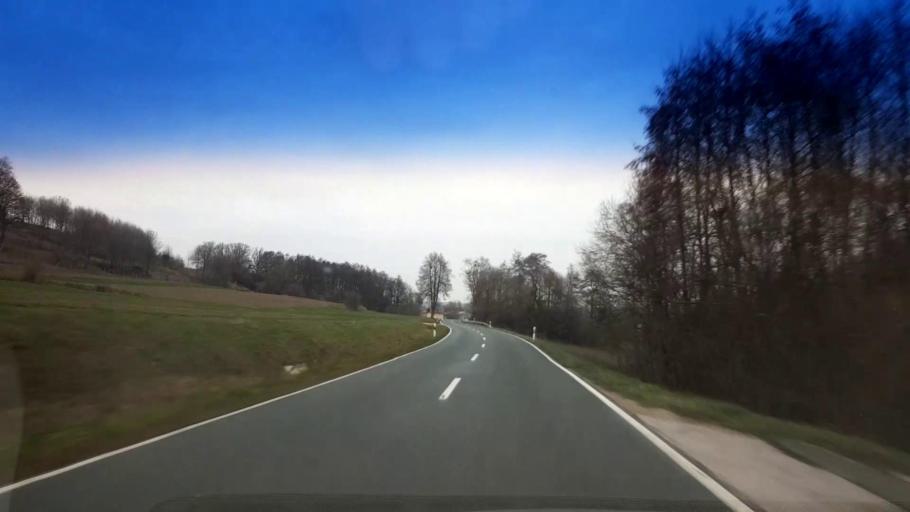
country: DE
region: Bavaria
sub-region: Upper Franconia
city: Altendorf
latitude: 49.7828
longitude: 11.0071
